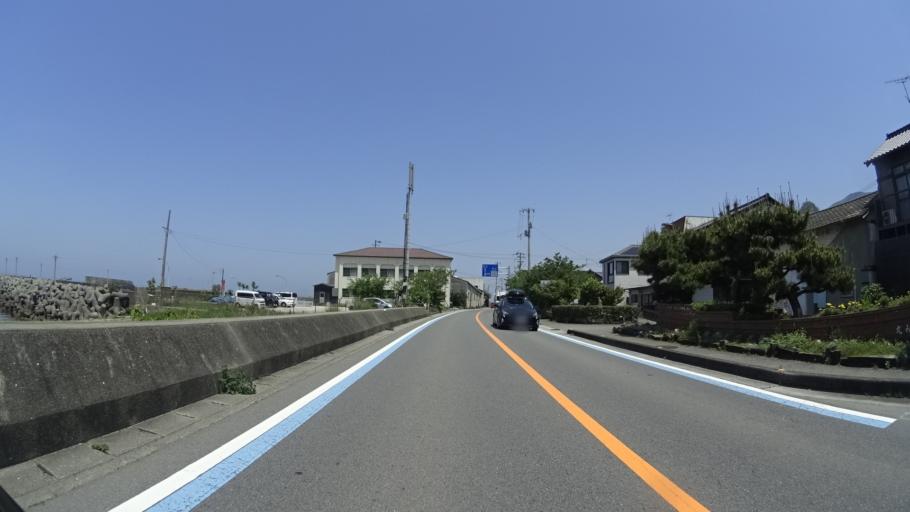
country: JP
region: Ehime
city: Iyo
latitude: 33.6872
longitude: 132.6365
